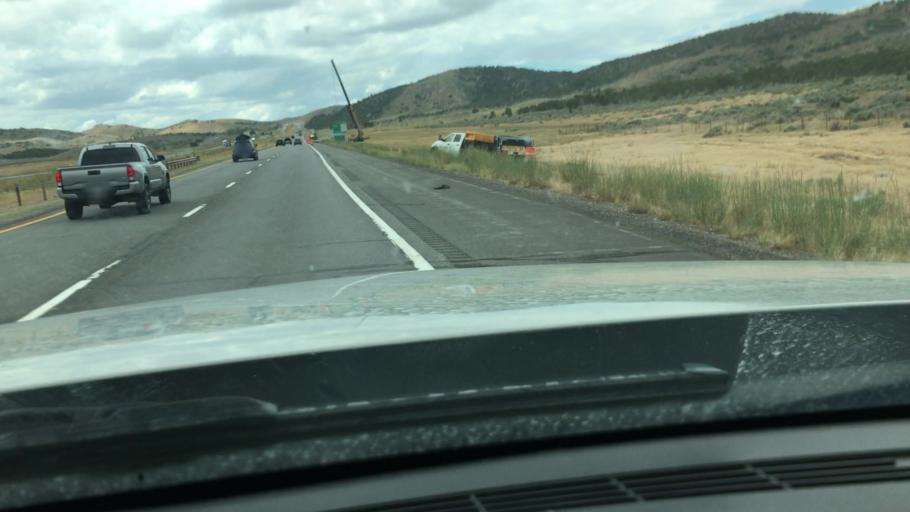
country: US
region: Utah
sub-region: Beaver County
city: Beaver
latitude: 38.6653
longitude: -112.5910
